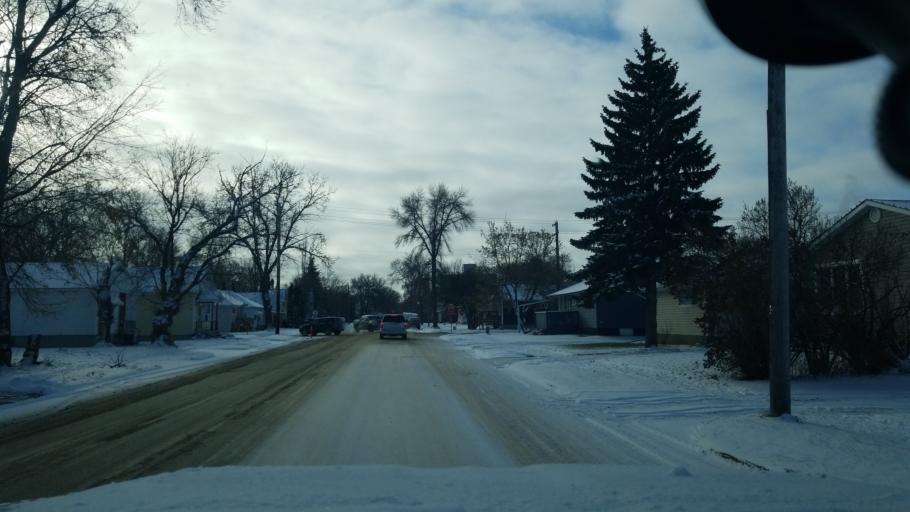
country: CA
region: Manitoba
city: Portage la Prairie
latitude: 49.9763
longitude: -98.3012
